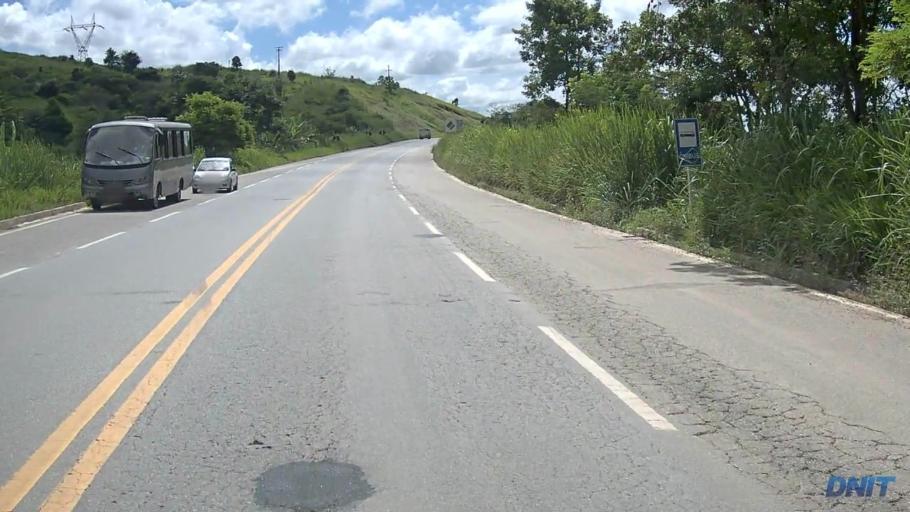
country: BR
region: Minas Gerais
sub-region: Governador Valadares
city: Governador Valadares
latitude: -19.0170
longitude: -42.1416
